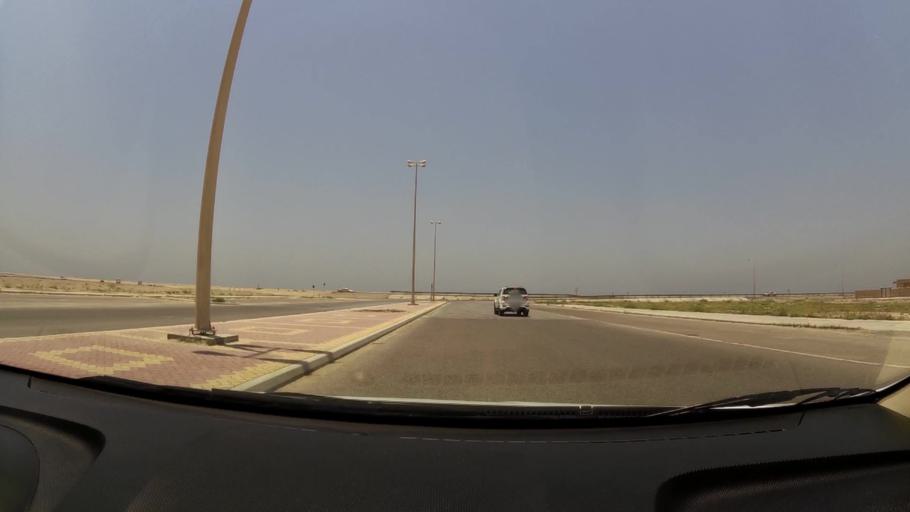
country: AE
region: Umm al Qaywayn
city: Umm al Qaywayn
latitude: 25.5780
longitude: 55.5549
